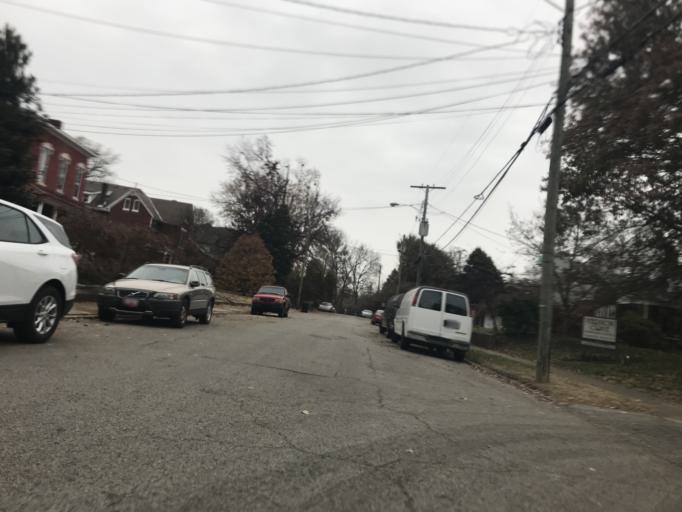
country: US
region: Indiana
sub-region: Clark County
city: Jeffersonville
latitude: 38.2567
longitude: -85.7071
